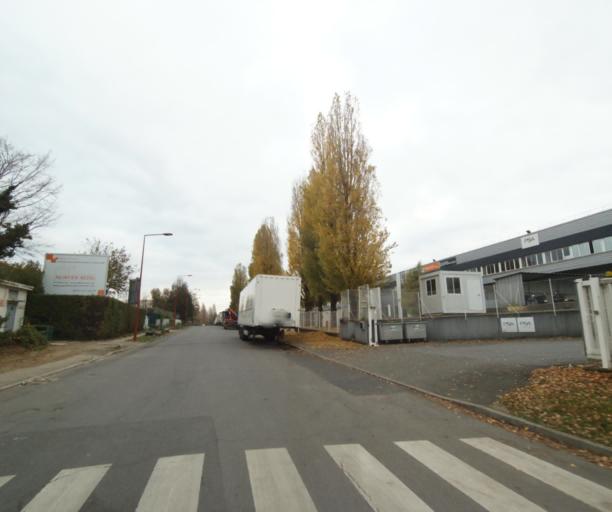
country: FR
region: Ile-de-France
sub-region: Departement du Val-d'Oise
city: Gonesse
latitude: 48.9837
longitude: 2.4597
